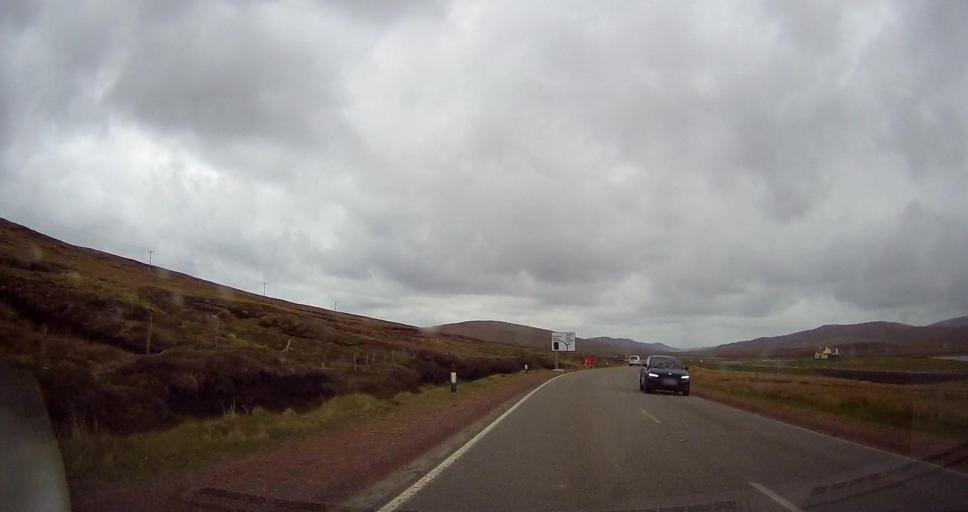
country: GB
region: Scotland
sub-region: Shetland Islands
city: Lerwick
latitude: 60.2819
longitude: -1.2440
